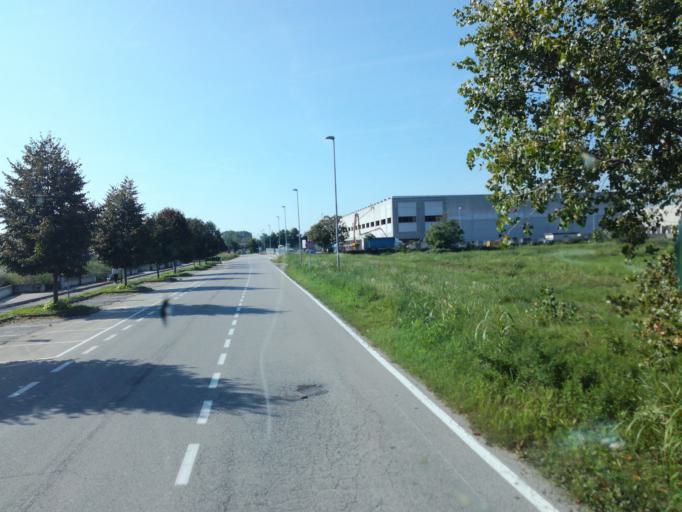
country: IT
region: Lombardy
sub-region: Provincia di Lodi
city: Tavazzano
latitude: 45.3313
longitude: 9.3940
